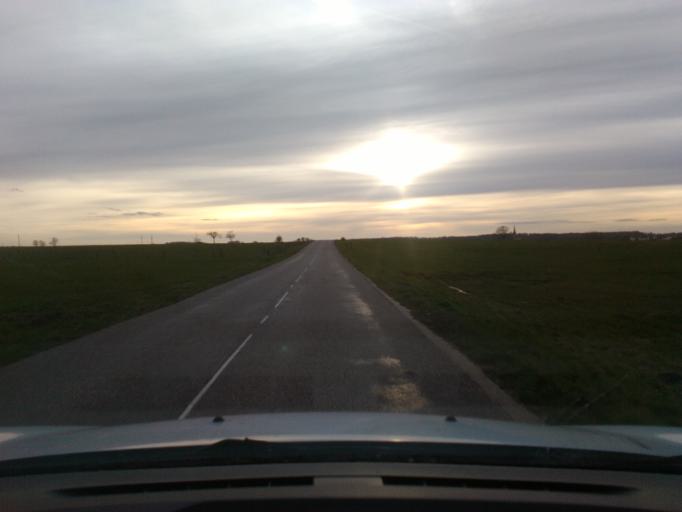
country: FR
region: Lorraine
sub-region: Departement des Vosges
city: Chatel-sur-Moselle
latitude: 48.3501
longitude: 6.4479
